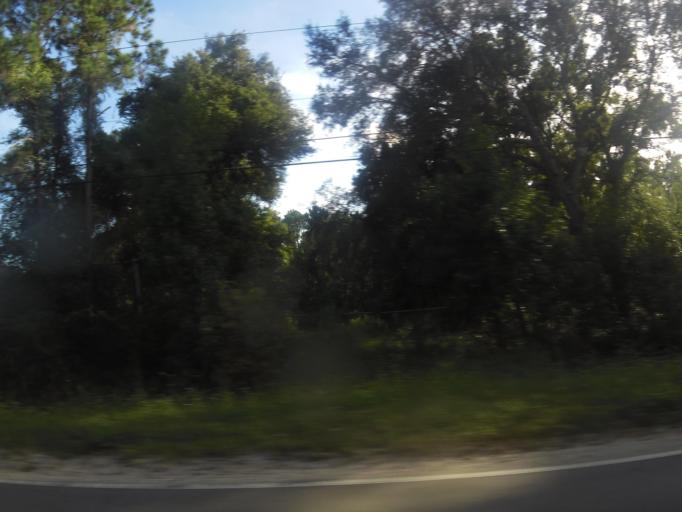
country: US
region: Florida
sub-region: Clay County
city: Green Cove Springs
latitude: 29.9147
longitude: -81.5334
